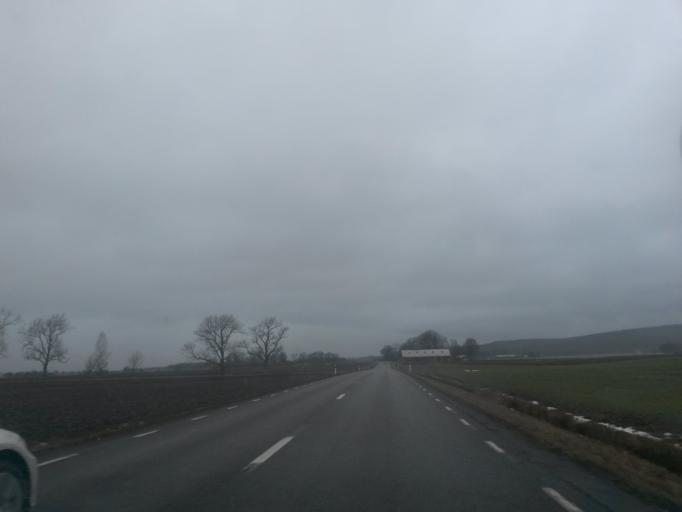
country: SE
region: Vaestra Goetaland
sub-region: Vanersborgs Kommun
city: Vargon
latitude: 58.2725
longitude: 12.3996
